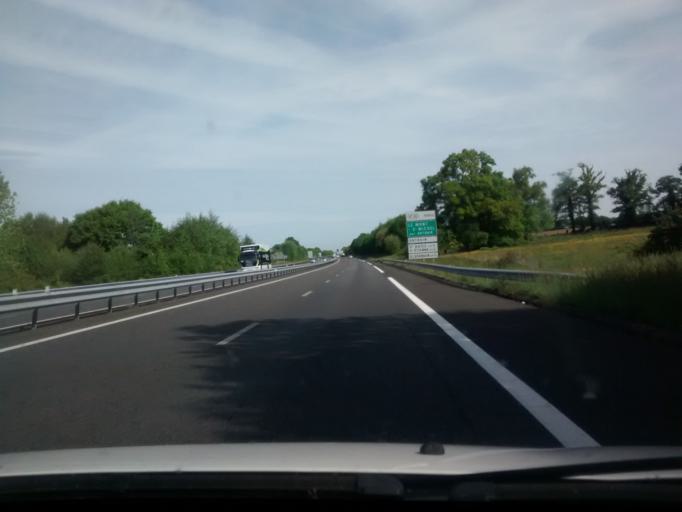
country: FR
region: Brittany
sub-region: Departement d'Ille-et-Vilaine
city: Saint-Etienne-en-Cogles
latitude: 48.3843
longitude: -1.3049
